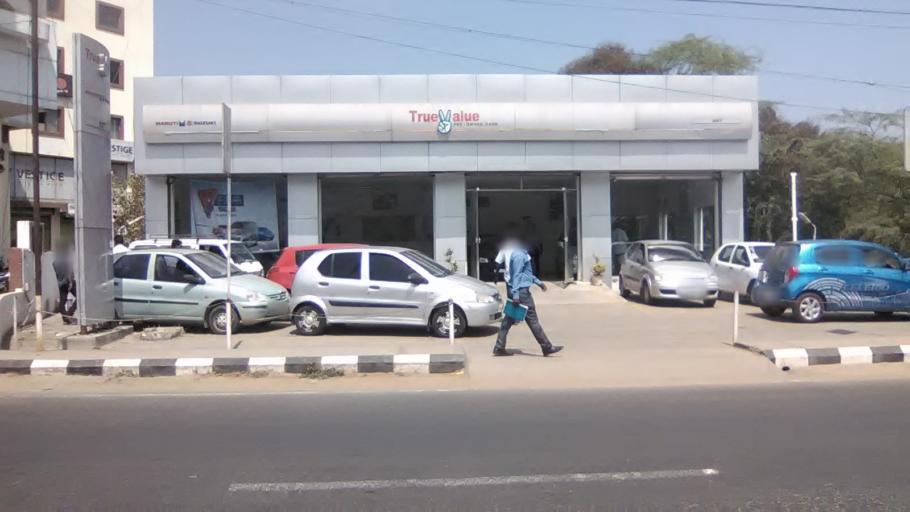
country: IN
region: Tamil Nadu
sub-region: Tiruchchirappalli
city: Tiruchirappalli
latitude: 10.8039
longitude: 78.6779
